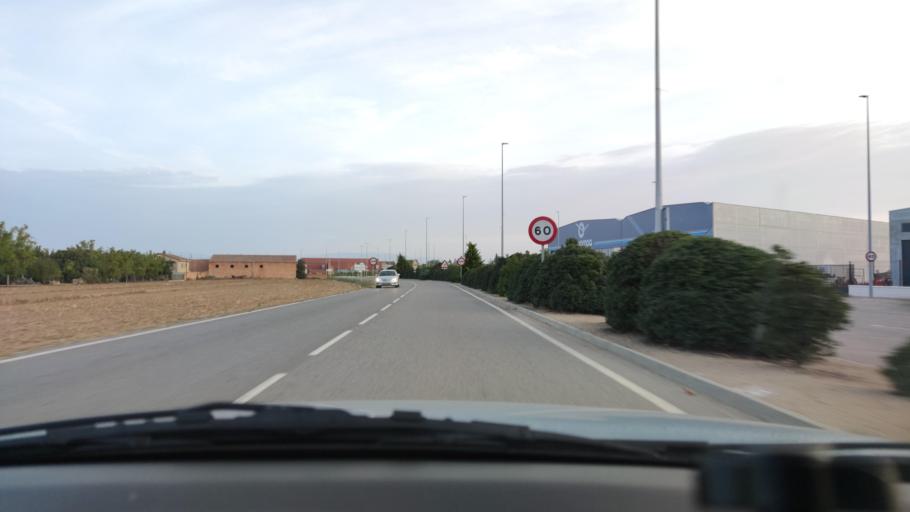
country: ES
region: Catalonia
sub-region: Provincia de Lleida
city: Mollerussa
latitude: 41.6451
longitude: 0.8767
